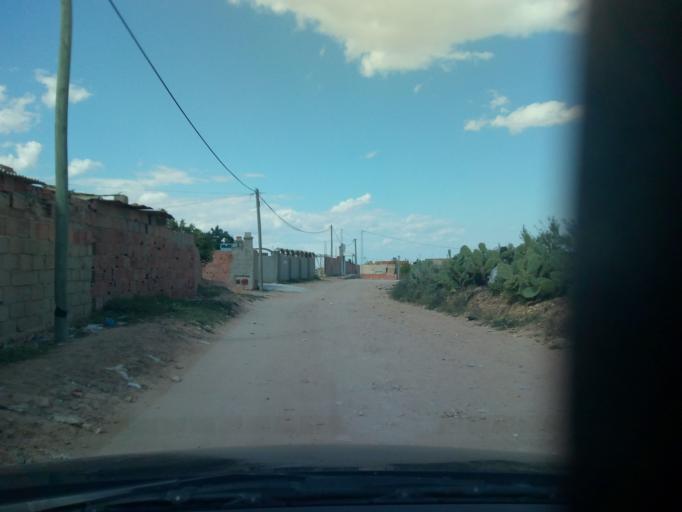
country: TN
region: Safaqis
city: Sfax
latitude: 34.7255
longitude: 10.6077
